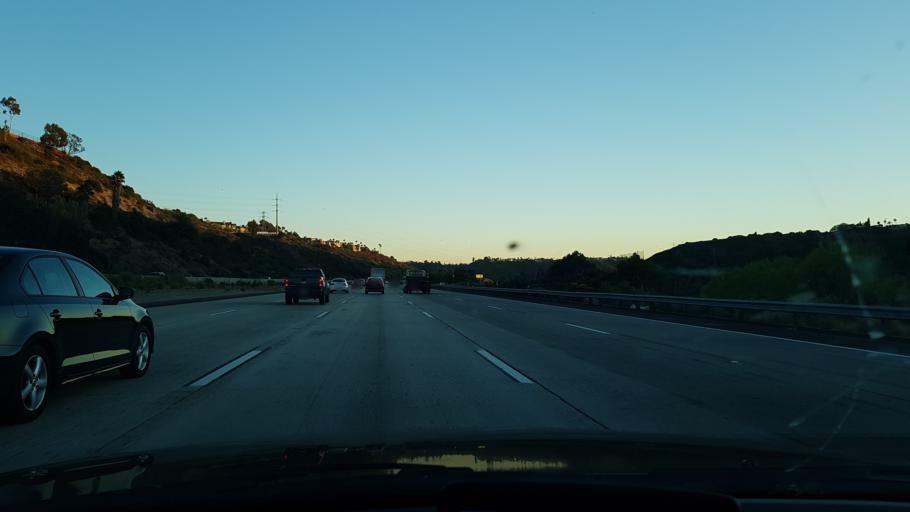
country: US
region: California
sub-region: San Diego County
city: La Mesa
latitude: 32.8016
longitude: -117.1130
